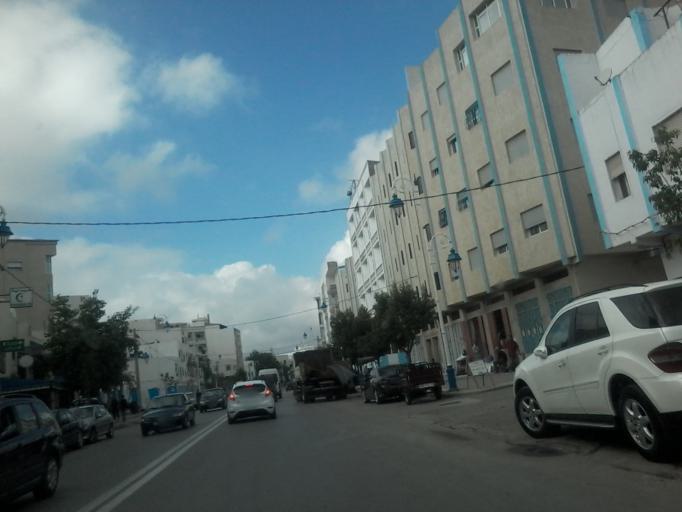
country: MA
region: Tanger-Tetouan
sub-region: Tetouan
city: Martil
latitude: 35.6267
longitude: -5.2792
